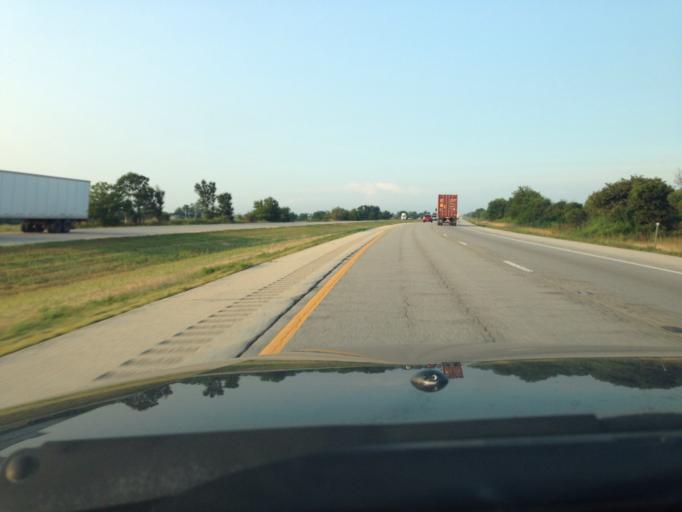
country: US
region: Illinois
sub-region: Ford County
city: Paxton
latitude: 40.5071
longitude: -88.0852
